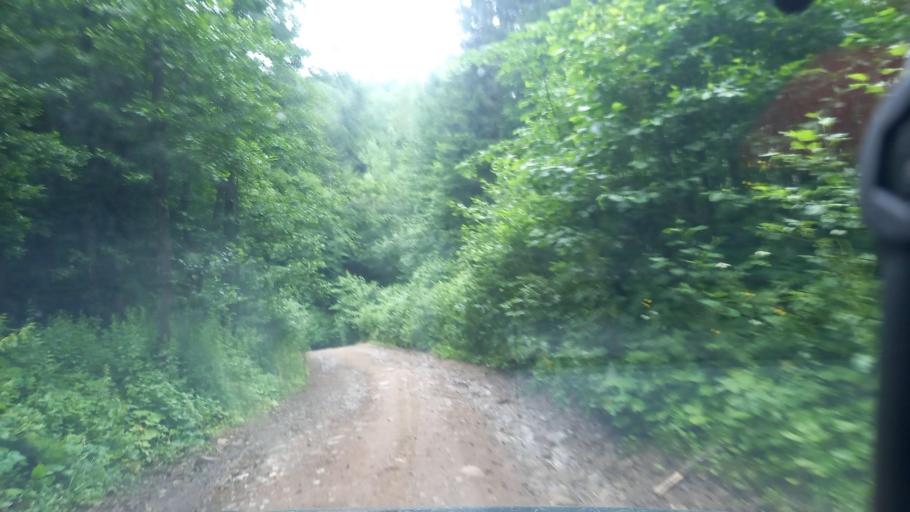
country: RU
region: Karachayevo-Cherkesiya
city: Kurdzhinovo
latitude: 43.8122
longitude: 40.8742
